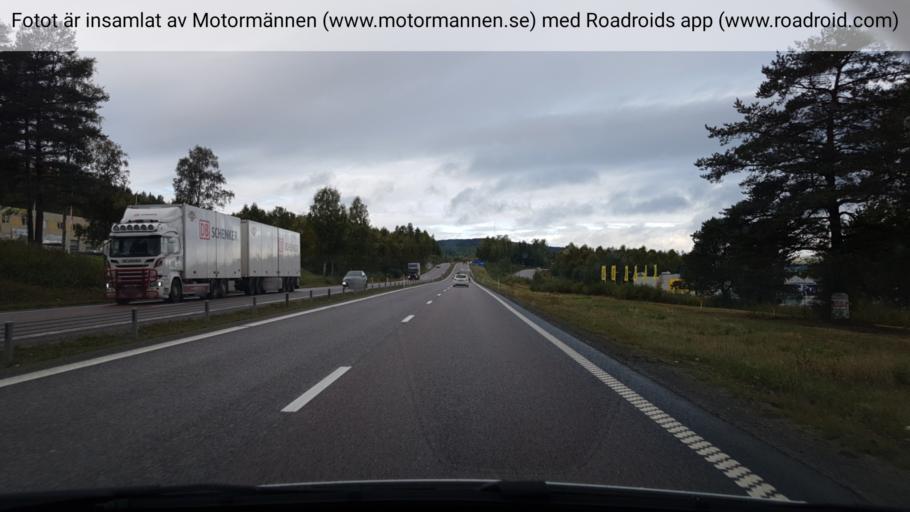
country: SE
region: Vaesternorrland
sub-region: OErnskoeldsviks Kommun
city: Ornskoldsvik
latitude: 63.3043
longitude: 18.7502
